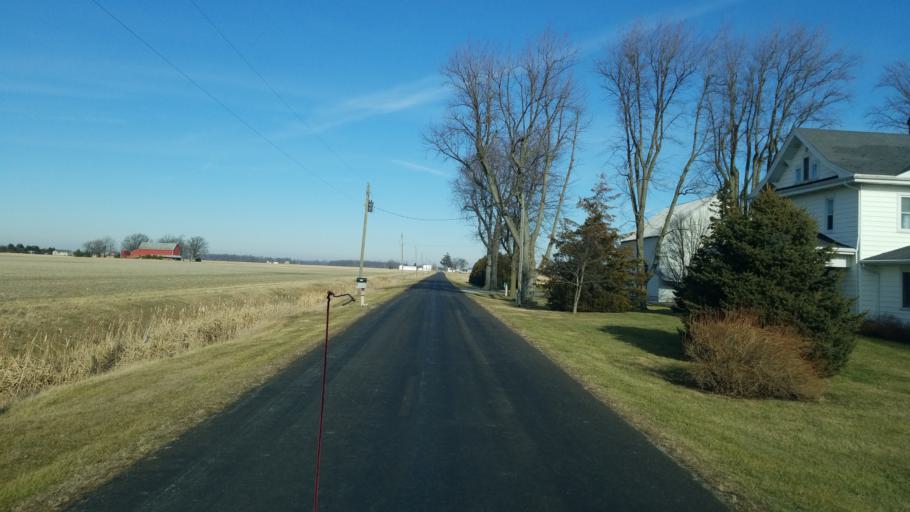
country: US
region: Ohio
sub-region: Putnam County
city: Pandora
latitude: 40.9705
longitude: -83.9382
